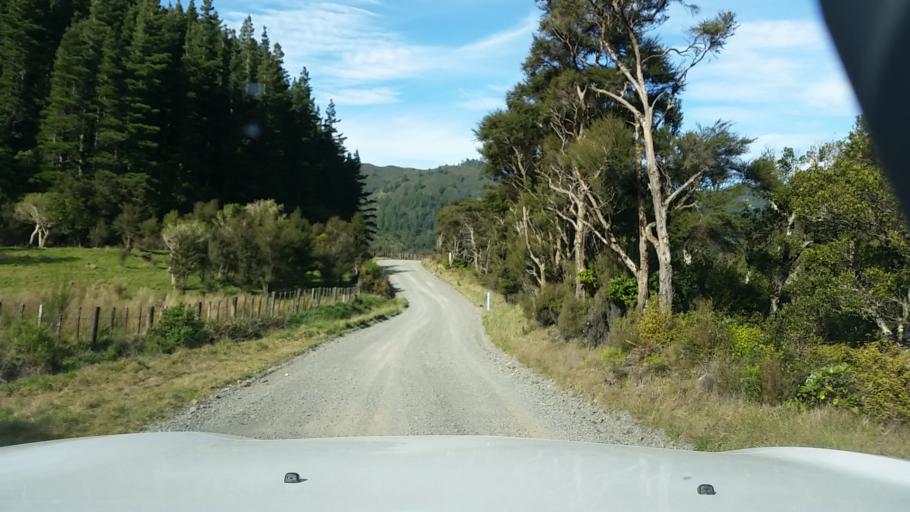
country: NZ
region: Wellington
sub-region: Masterton District
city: Masterton
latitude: -41.0081
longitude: 175.3915
